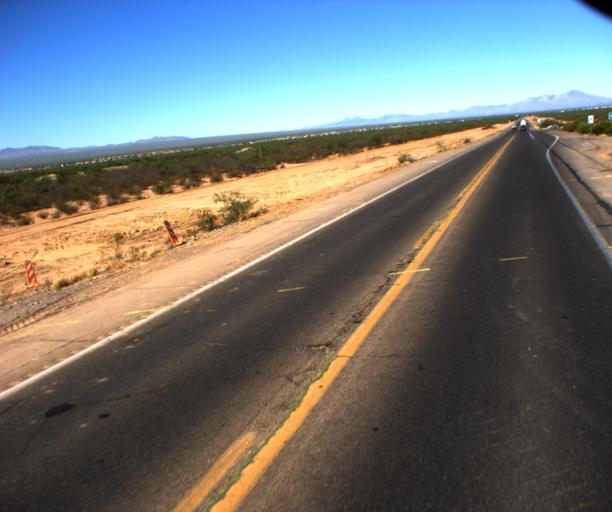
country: US
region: Arizona
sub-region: Pima County
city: Valencia West
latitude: 32.1554
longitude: -111.1135
